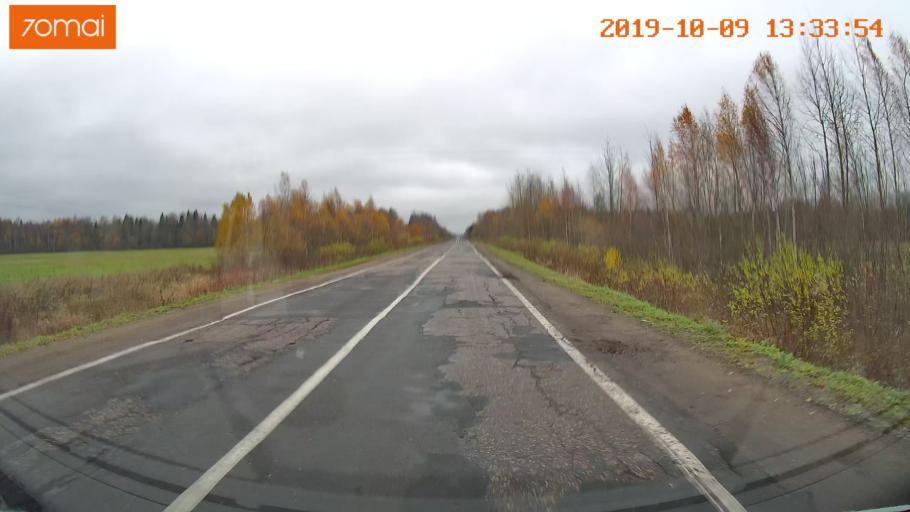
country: RU
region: Jaroslavl
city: Lyubim
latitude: 58.3277
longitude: 41.0538
